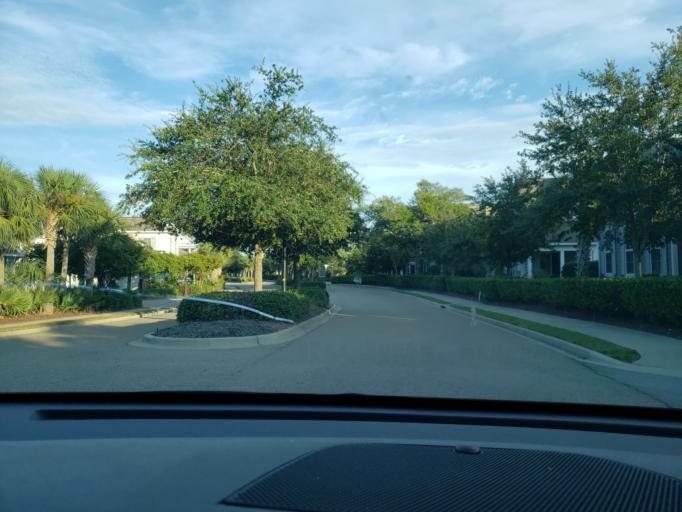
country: US
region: South Carolina
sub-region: Horry County
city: North Myrtle Beach
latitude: 33.7940
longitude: -78.7399
